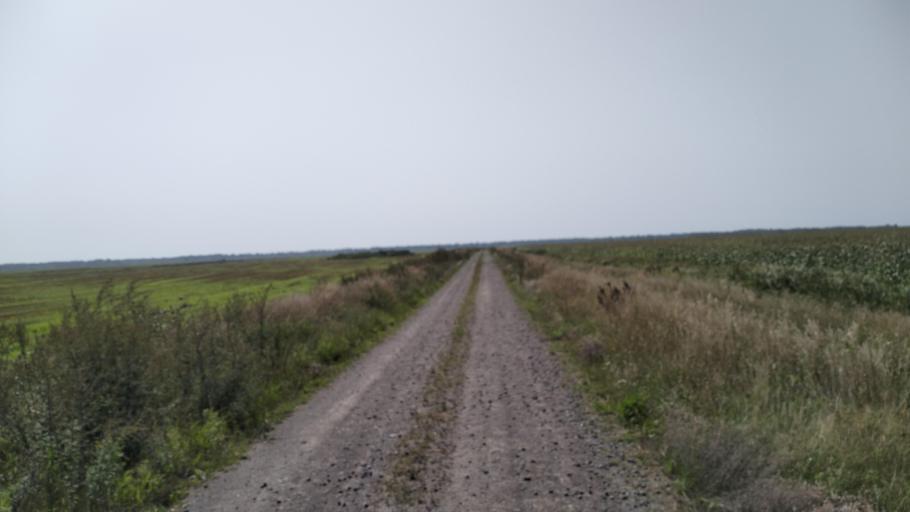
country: BY
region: Brest
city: Davyd-Haradok
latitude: 51.9914
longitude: 27.1644
